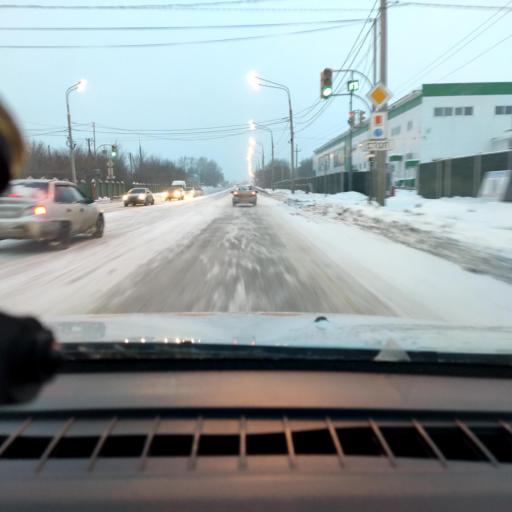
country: RU
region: Samara
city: Otradnyy
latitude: 53.3615
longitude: 51.3492
